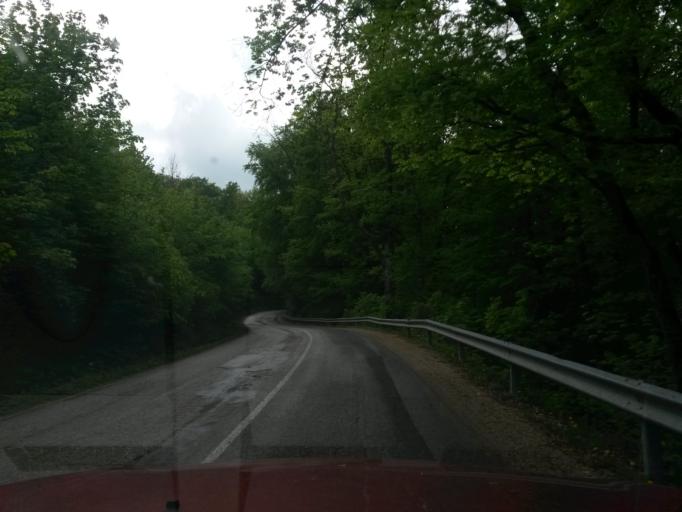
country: SK
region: Kosicky
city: Roznava
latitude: 48.5626
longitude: 20.4789
